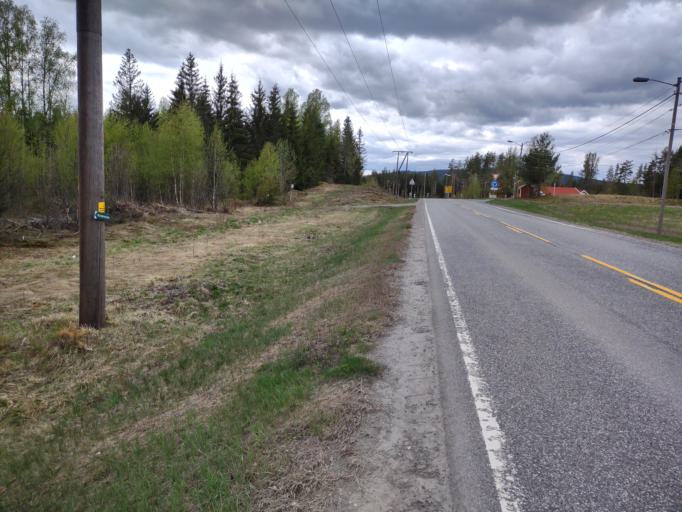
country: NO
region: Akershus
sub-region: Nannestad
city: Maura
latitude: 60.2531
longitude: 11.1034
